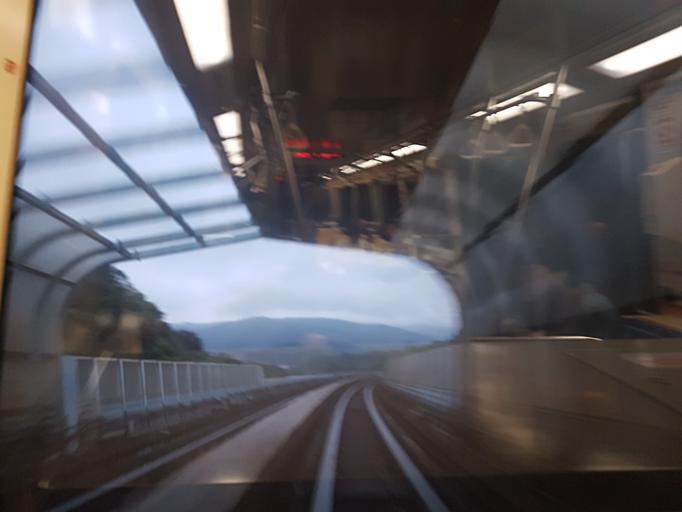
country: TW
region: Taipei
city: Taipei
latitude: 25.0767
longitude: 121.6070
